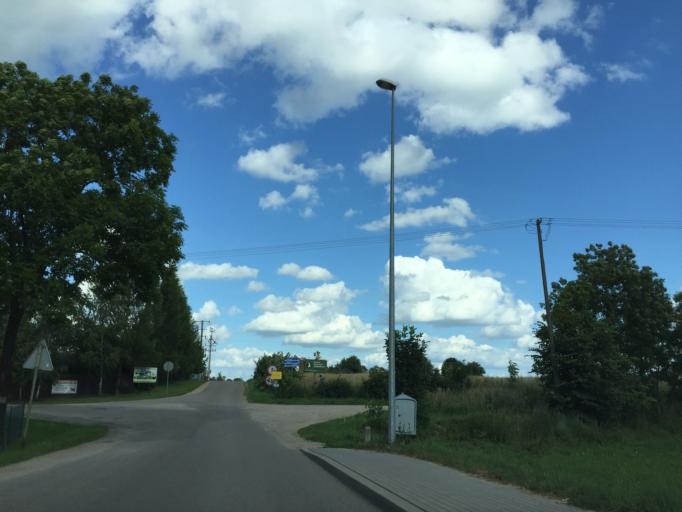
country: PL
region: Podlasie
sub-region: Suwalki
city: Suwalki
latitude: 54.1241
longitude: 23.0295
